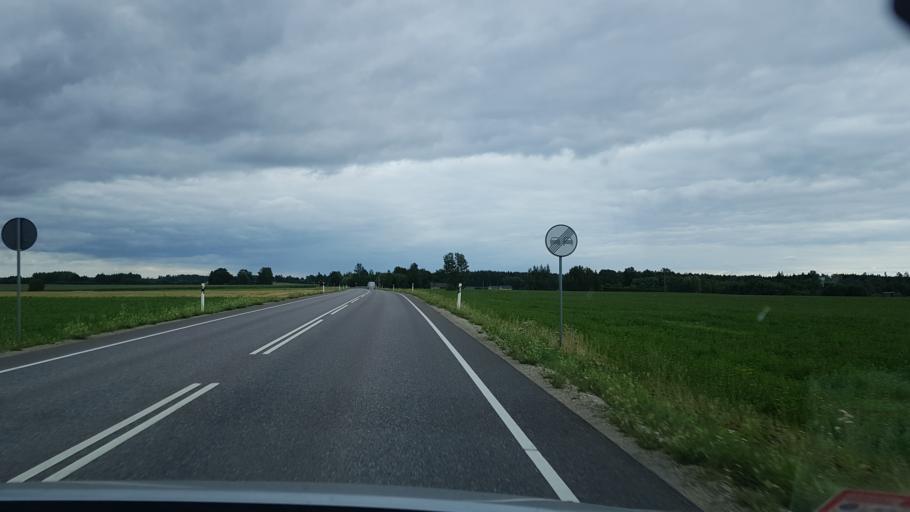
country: EE
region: Tartu
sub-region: Tartu linn
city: Tartu
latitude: 58.4288
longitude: 26.8485
